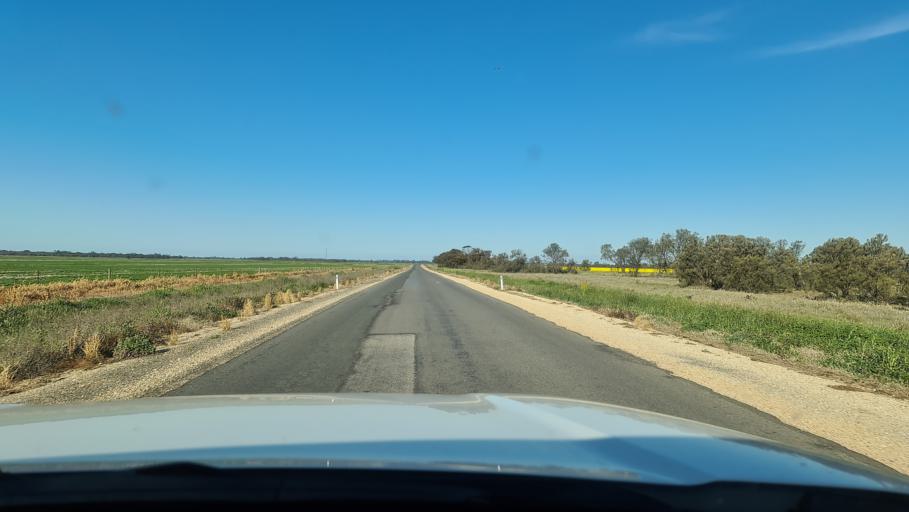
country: AU
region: Victoria
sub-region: Horsham
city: Horsham
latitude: -36.4492
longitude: 142.5606
